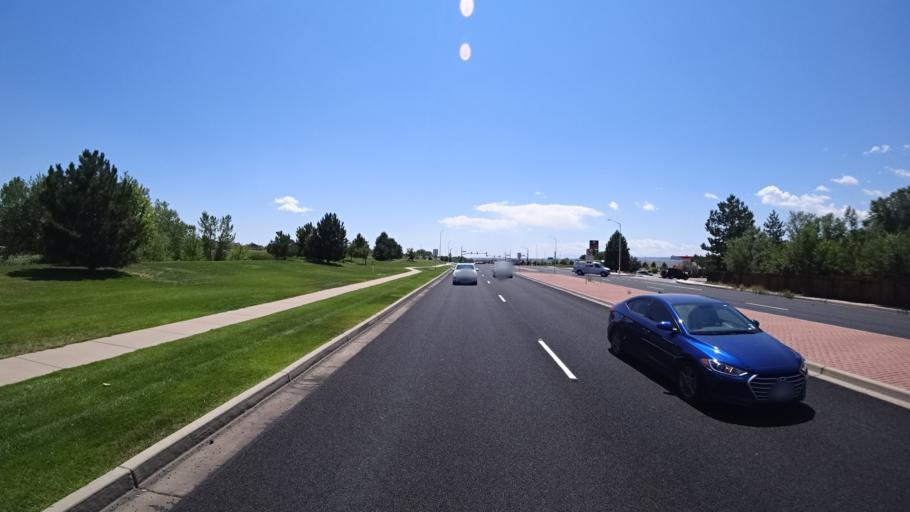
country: US
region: Colorado
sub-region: El Paso County
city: Stratmoor
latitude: 38.7827
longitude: -104.7388
